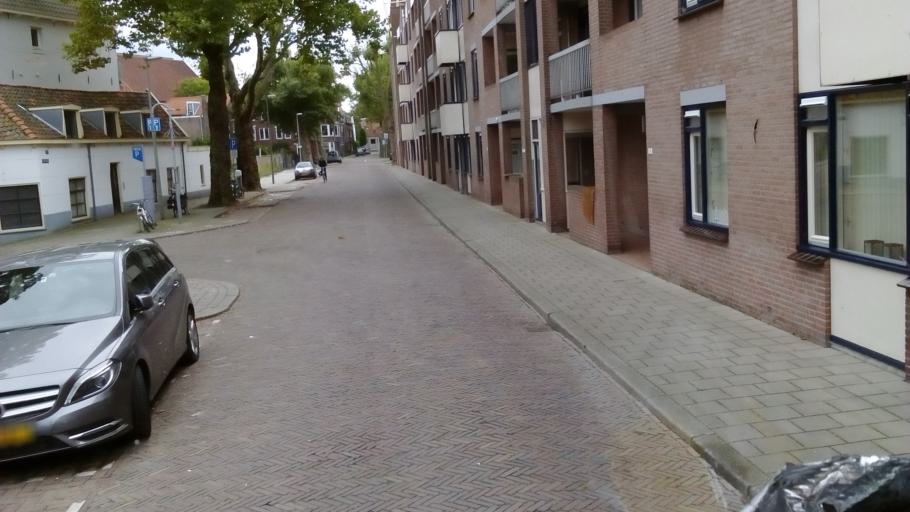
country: NL
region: South Holland
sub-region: Gemeente Schiedam
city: Schiedam
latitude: 51.9168
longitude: 4.3937
